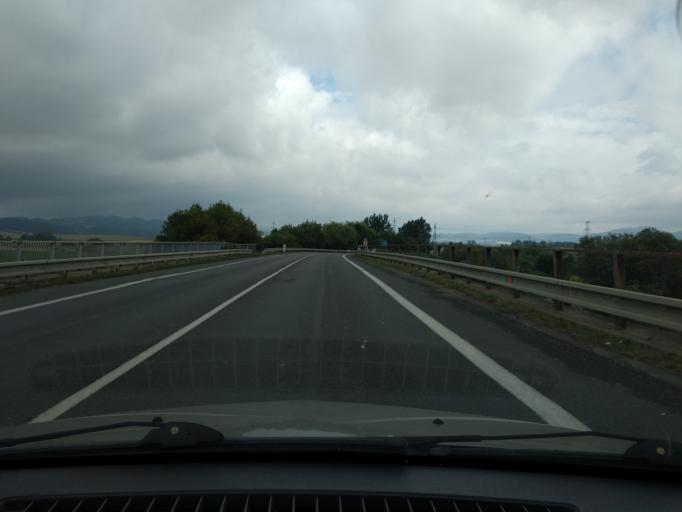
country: CZ
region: Olomoucky
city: Zabreh
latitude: 49.8873
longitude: 16.8923
